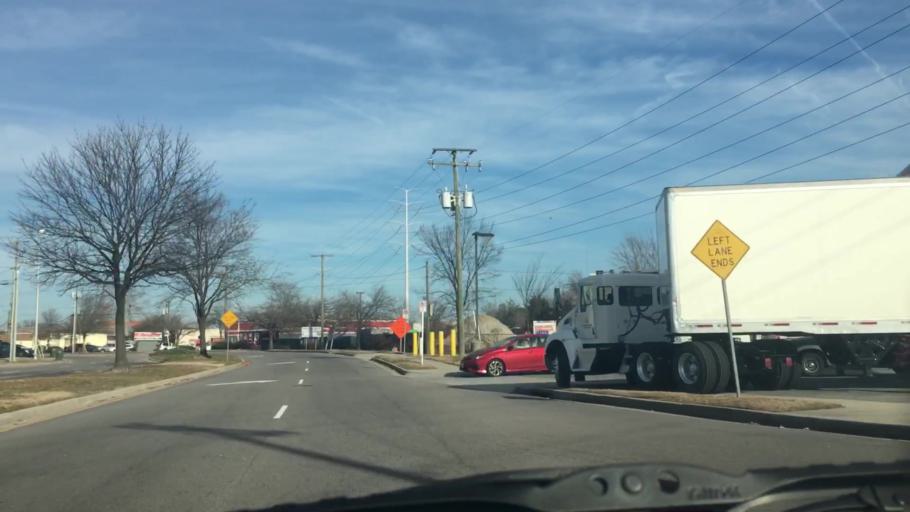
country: US
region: Virginia
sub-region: City of Norfolk
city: Norfolk
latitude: 36.8767
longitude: -76.2521
